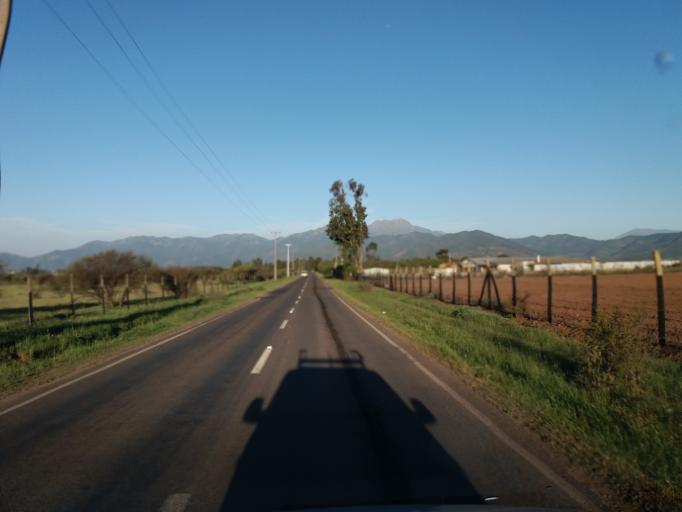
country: CL
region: Valparaiso
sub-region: Provincia de Quillota
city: Quillota
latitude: -32.9168
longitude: -71.3285
